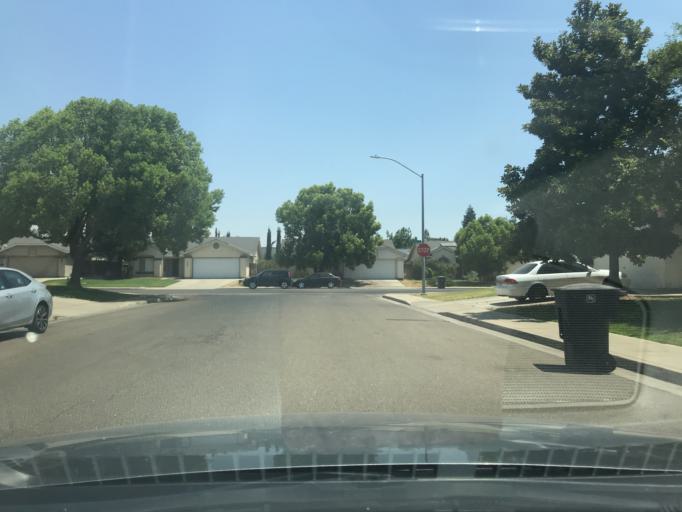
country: US
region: California
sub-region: Merced County
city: Atwater
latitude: 37.3634
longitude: -120.6013
